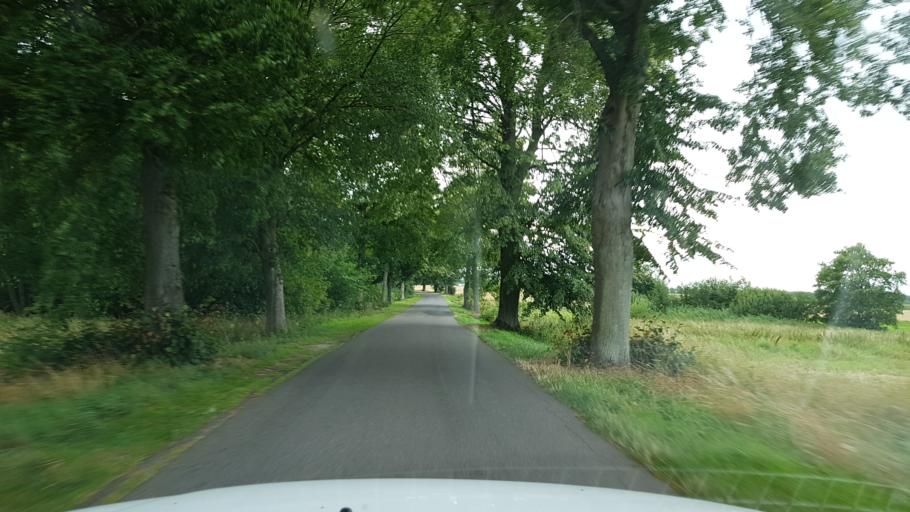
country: PL
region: West Pomeranian Voivodeship
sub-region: Powiat bialogardzki
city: Karlino
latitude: 54.1160
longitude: 15.8652
